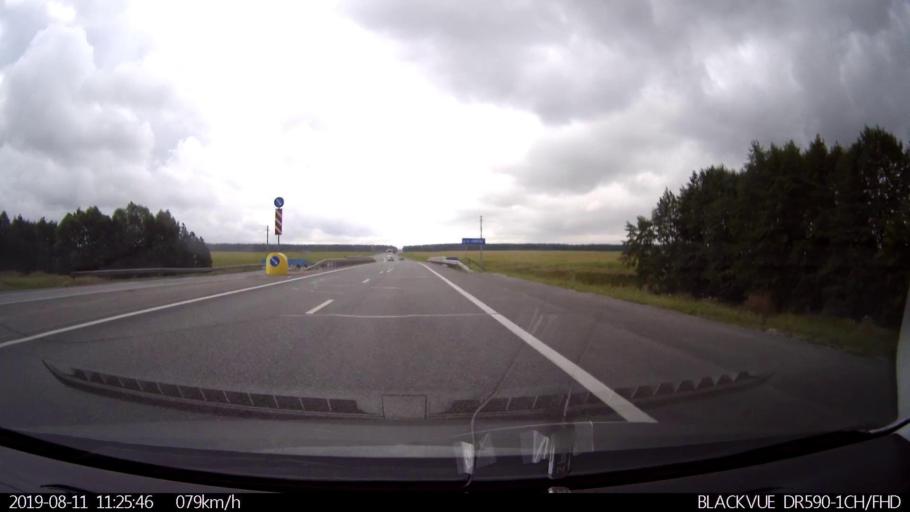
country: RU
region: Ulyanovsk
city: Krasnyy Gulyay
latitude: 54.1134
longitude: 48.2371
